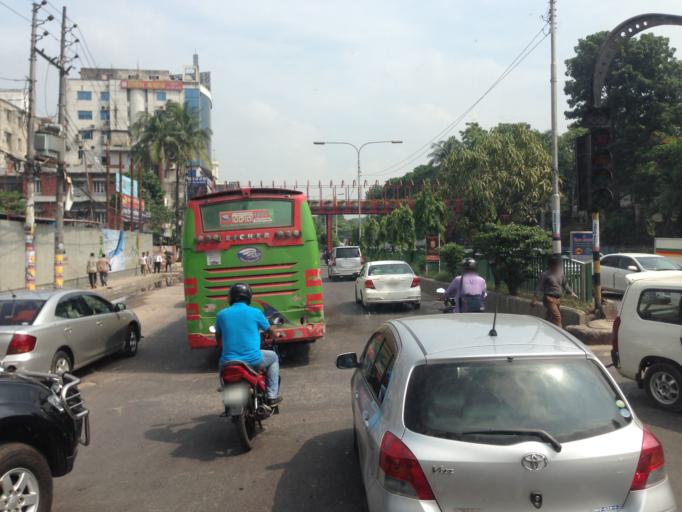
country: BD
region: Dhaka
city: Azimpur
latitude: 23.7564
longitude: 90.3751
